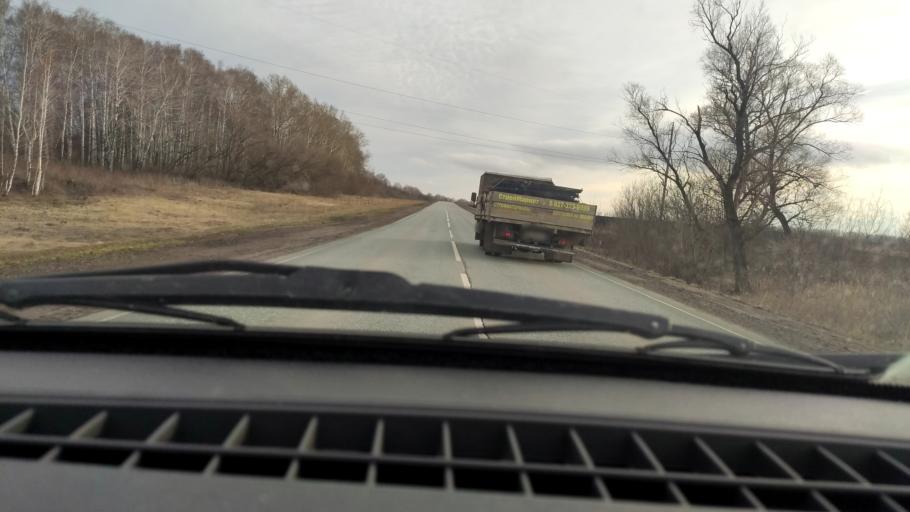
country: RU
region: Bashkortostan
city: Chishmy
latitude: 54.5112
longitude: 55.2921
